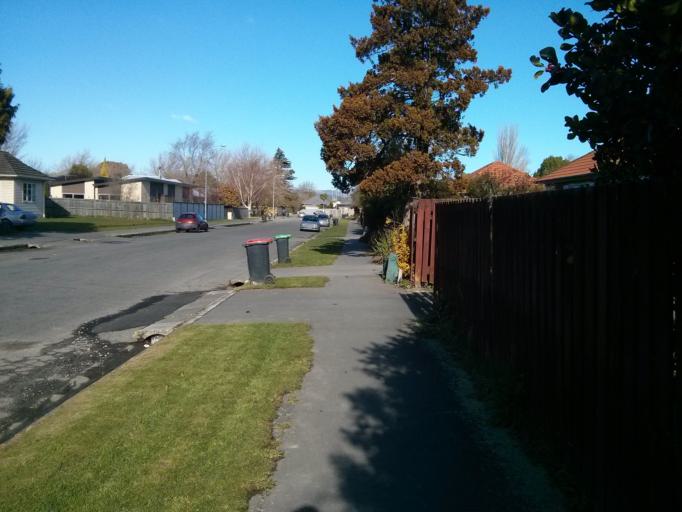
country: NZ
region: Canterbury
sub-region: Christchurch City
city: Christchurch
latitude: -43.5311
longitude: 172.5884
